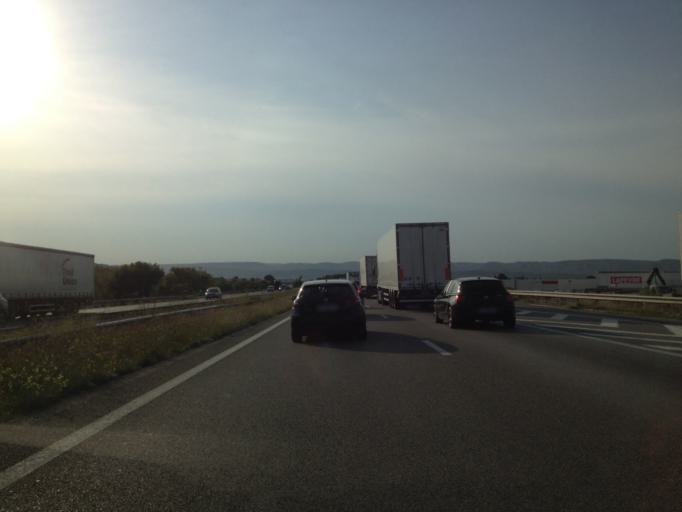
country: FR
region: Provence-Alpes-Cote d'Azur
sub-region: Departement des Bouches-du-Rhone
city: Vitrolles
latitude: 43.4456
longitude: 5.2428
